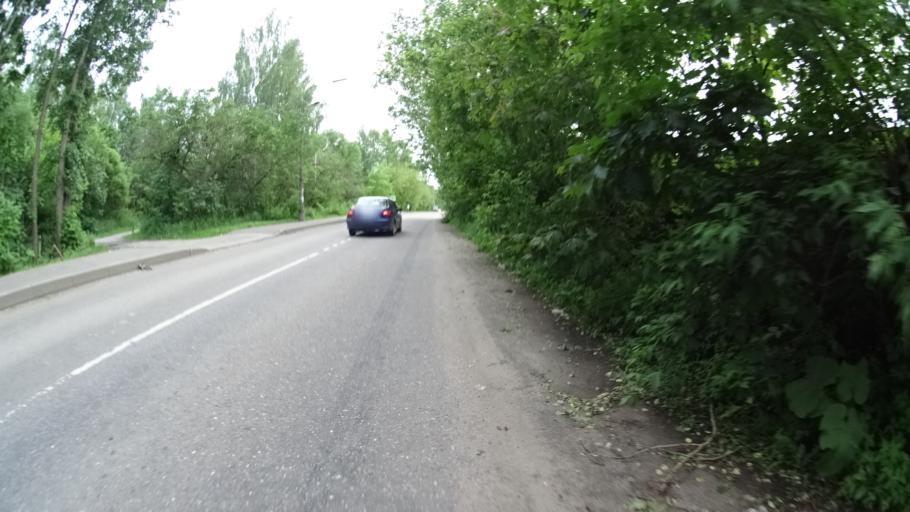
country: RU
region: Moskovskaya
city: Sofrino
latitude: 56.1318
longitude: 37.9355
